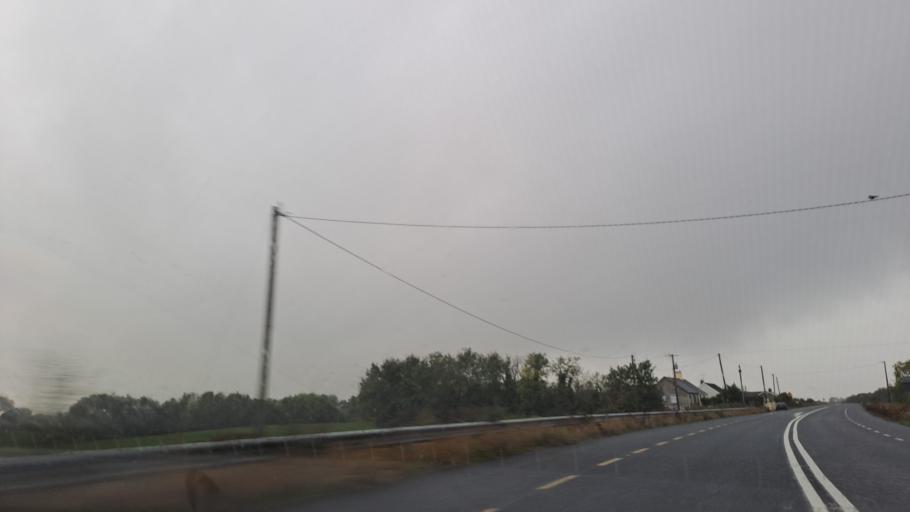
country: GB
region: Northern Ireland
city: Crossmaglen
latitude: 53.9721
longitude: -6.6064
